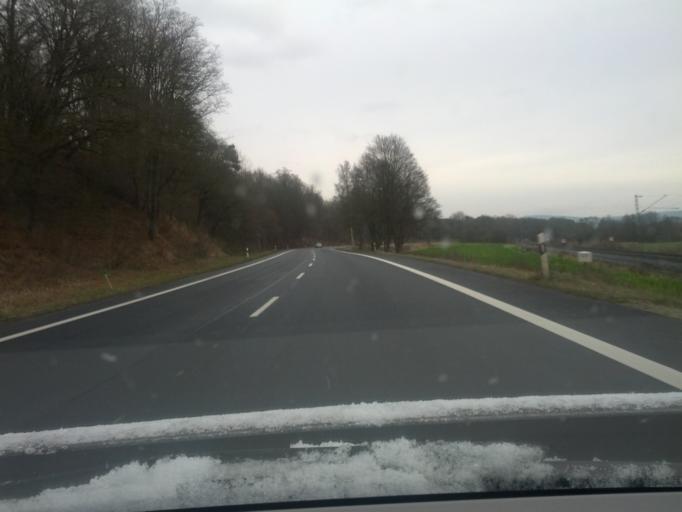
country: DE
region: Hesse
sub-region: Regierungsbezirk Kassel
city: Sontra
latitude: 51.1444
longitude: 9.9782
